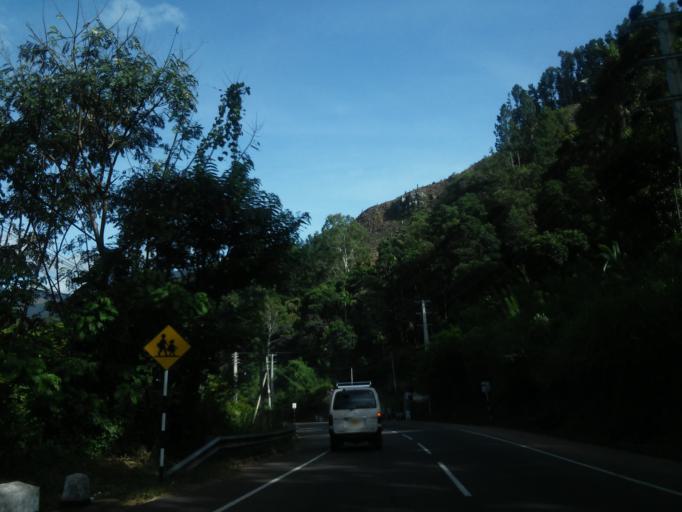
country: LK
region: Uva
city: Haputale
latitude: 6.7641
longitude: 80.8709
